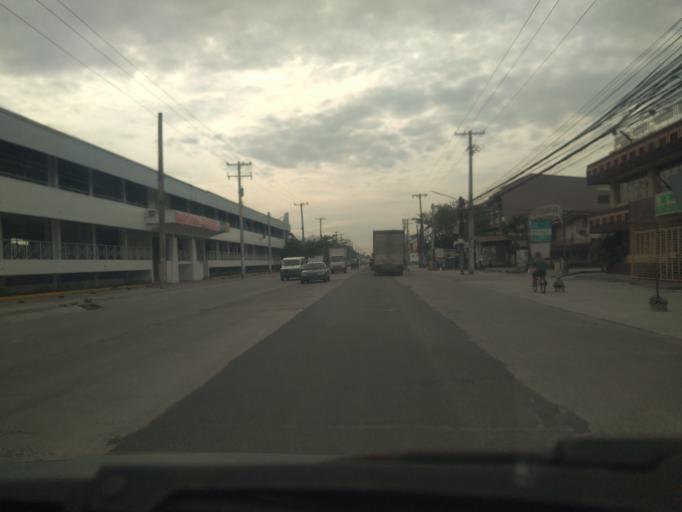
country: PH
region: Central Luzon
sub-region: Province of Pampanga
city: San Fernando
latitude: 15.0201
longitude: 120.7000
